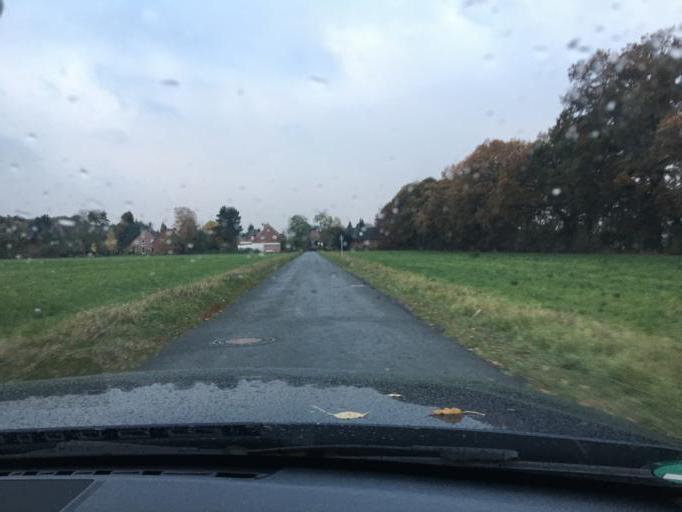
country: DE
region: North Rhine-Westphalia
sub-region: Regierungsbezirk Munster
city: Muenster
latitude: 51.9916
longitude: 7.6774
